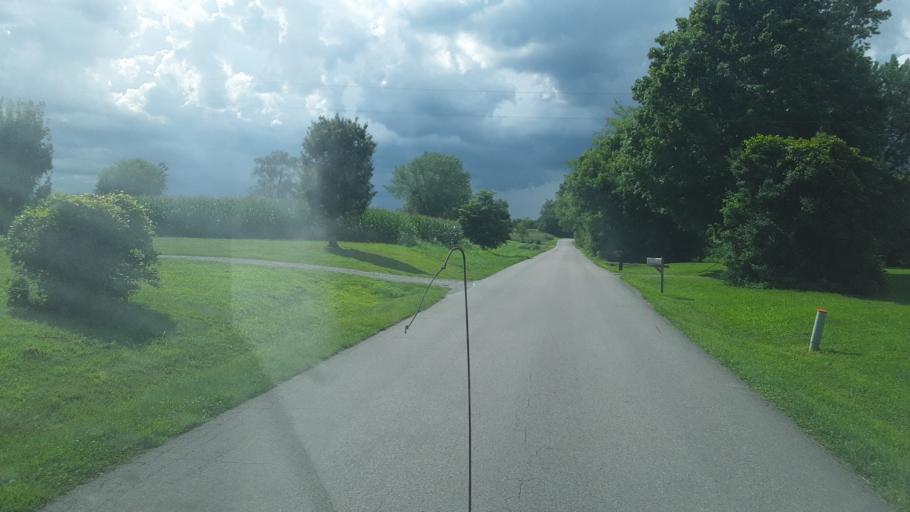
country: US
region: Kentucky
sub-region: Todd County
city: Elkton
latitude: 36.7434
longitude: -87.1667
